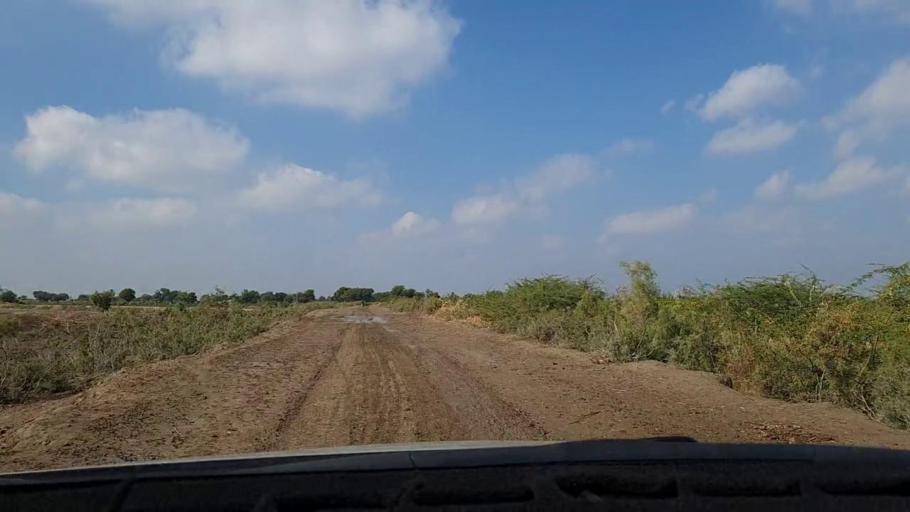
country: PK
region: Sindh
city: Tando Mittha Khan
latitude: 25.7750
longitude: 69.2576
